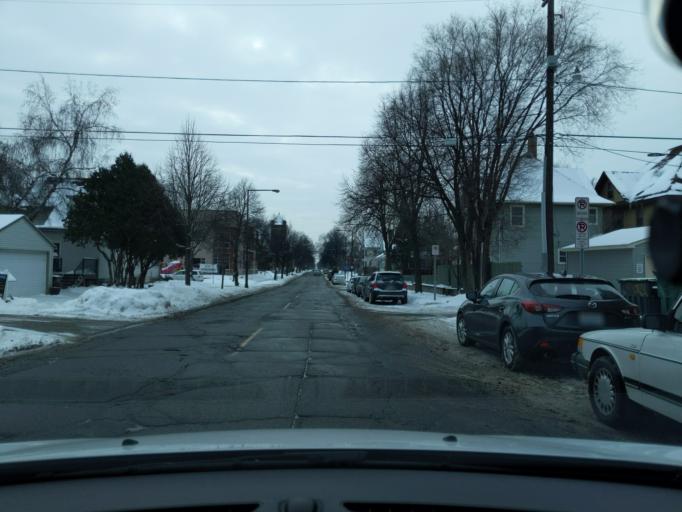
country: US
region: Minnesota
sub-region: Ramsey County
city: Saint Paul
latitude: 44.9464
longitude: -93.1365
